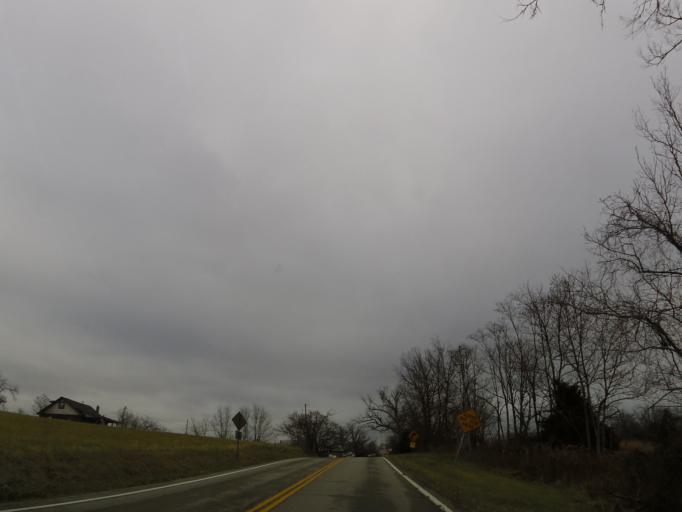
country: US
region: Kentucky
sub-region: Franklin County
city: Frankfort
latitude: 38.3439
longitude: -84.9663
